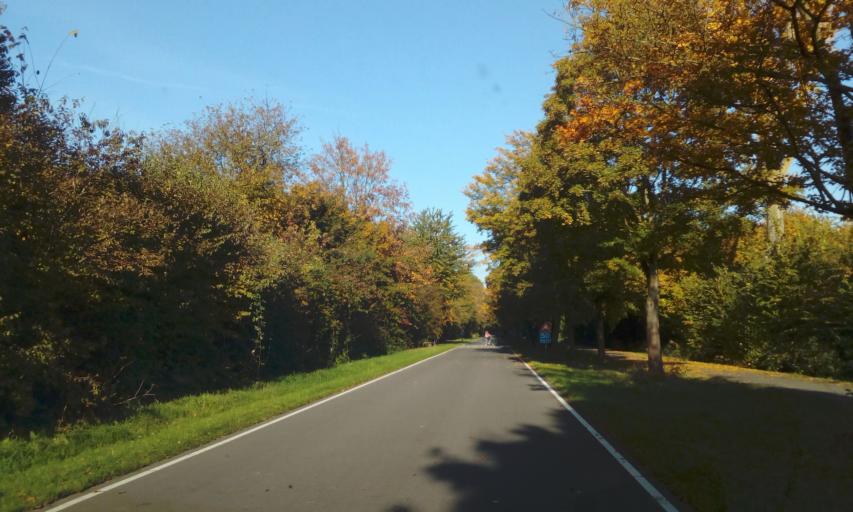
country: NL
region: South Holland
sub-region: Gemeente Lansingerland
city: Bleiswijk
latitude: 52.0064
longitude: 4.5468
